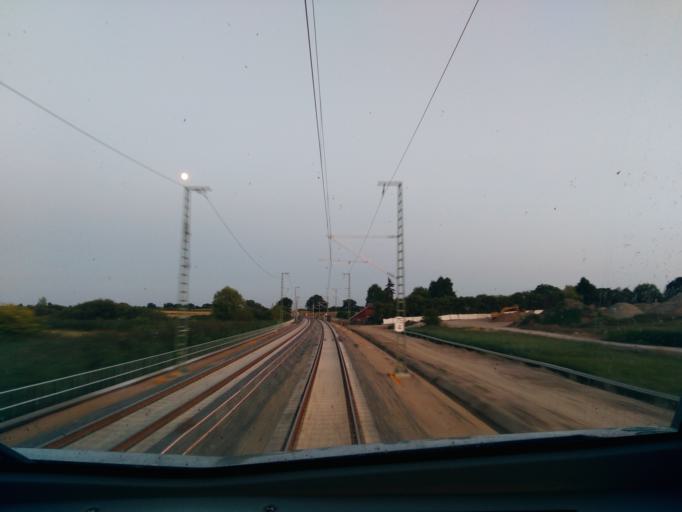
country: DE
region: Mecklenburg-Vorpommern
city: Lubstorf
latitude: 53.7145
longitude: 11.4098
